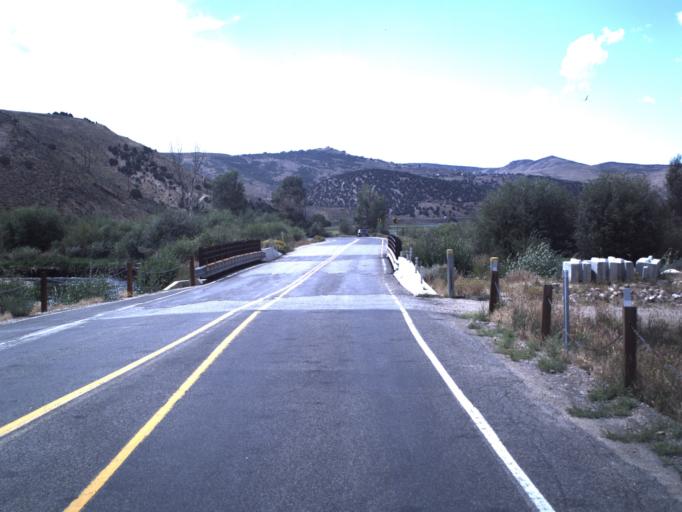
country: US
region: Utah
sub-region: Summit County
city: Oakley
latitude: 40.7541
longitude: -111.3732
